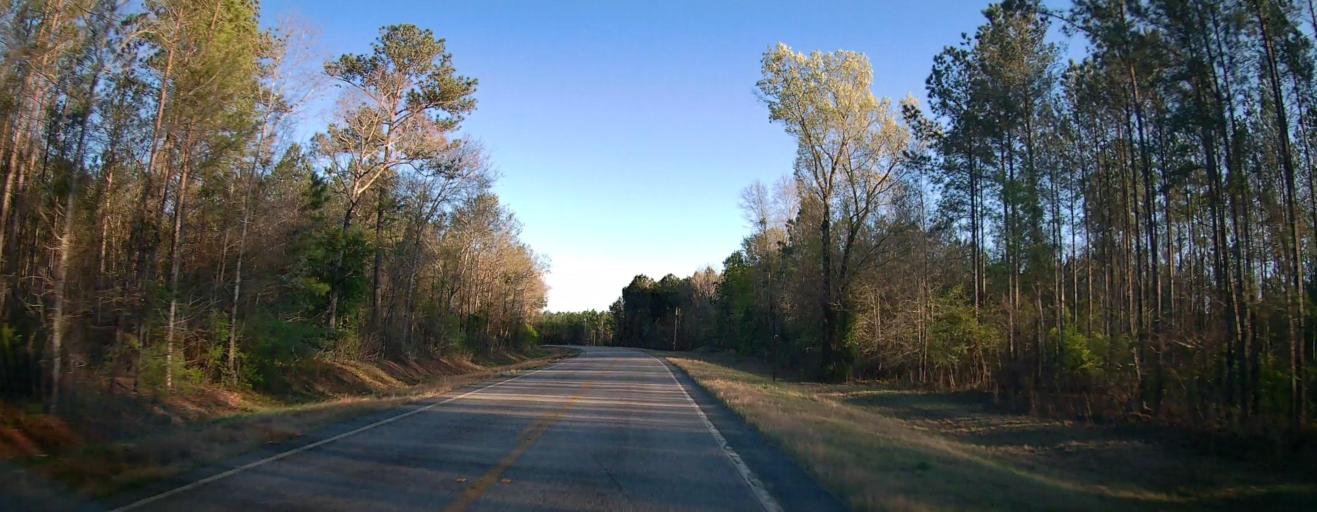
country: US
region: Georgia
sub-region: Wilcox County
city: Abbeville
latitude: 32.0721
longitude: -83.2836
